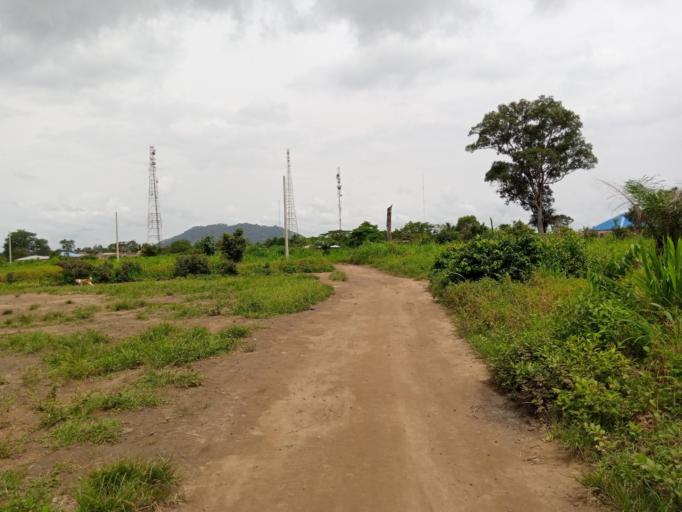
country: SL
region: Southern Province
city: Moyamba
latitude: 8.1686
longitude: -12.4166
